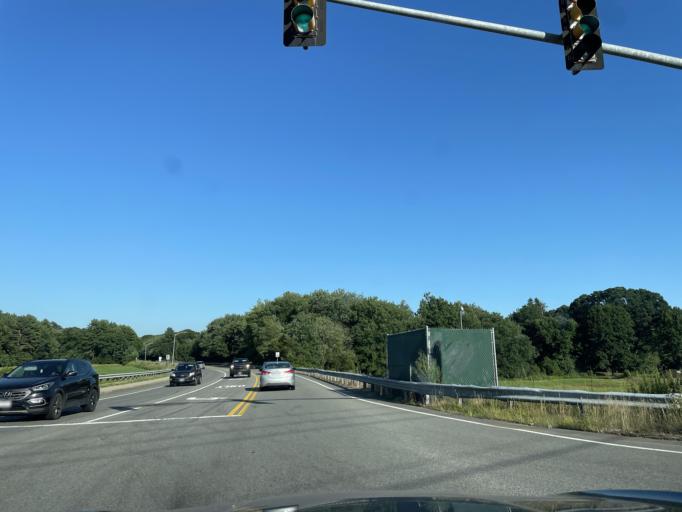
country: US
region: Massachusetts
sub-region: Bristol County
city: Mansfield Center
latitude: 42.0292
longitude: -71.1823
